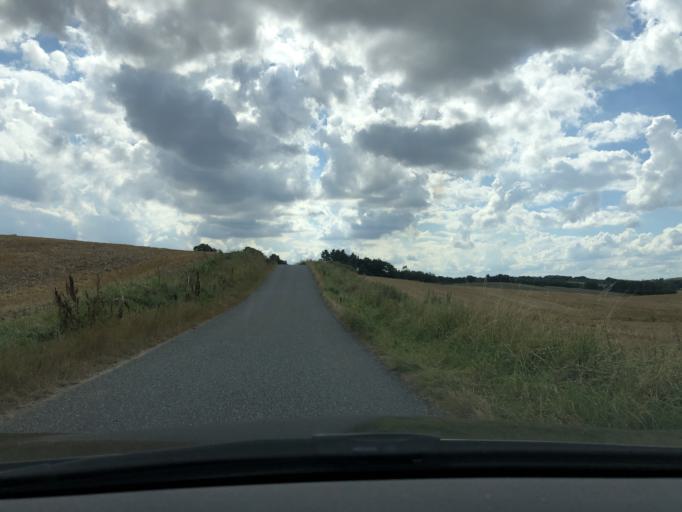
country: DK
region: South Denmark
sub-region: Vejle Kommune
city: Vejle
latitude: 55.7794
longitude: 9.5566
